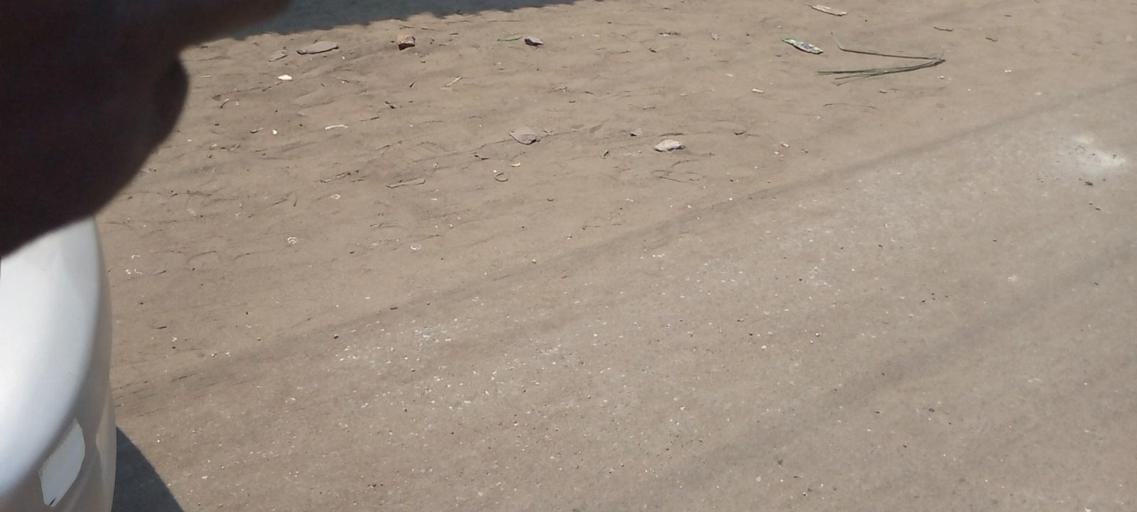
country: ZM
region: Lusaka
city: Lusaka
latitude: -15.4031
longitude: 28.3560
